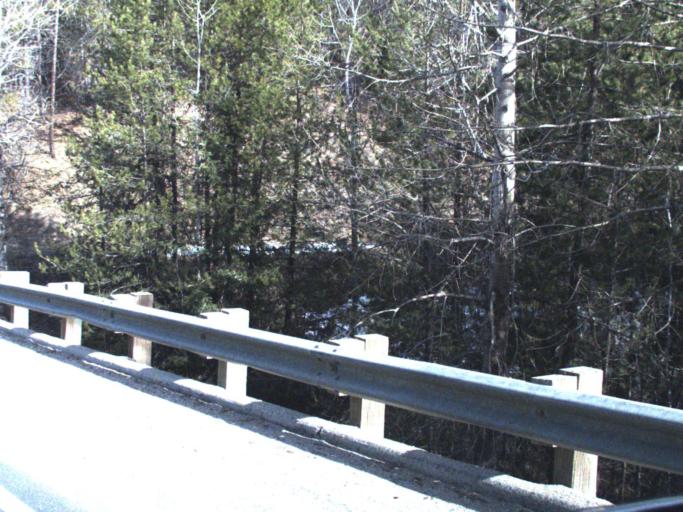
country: US
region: Washington
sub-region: Stevens County
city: Colville
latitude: 48.5091
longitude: -117.6756
